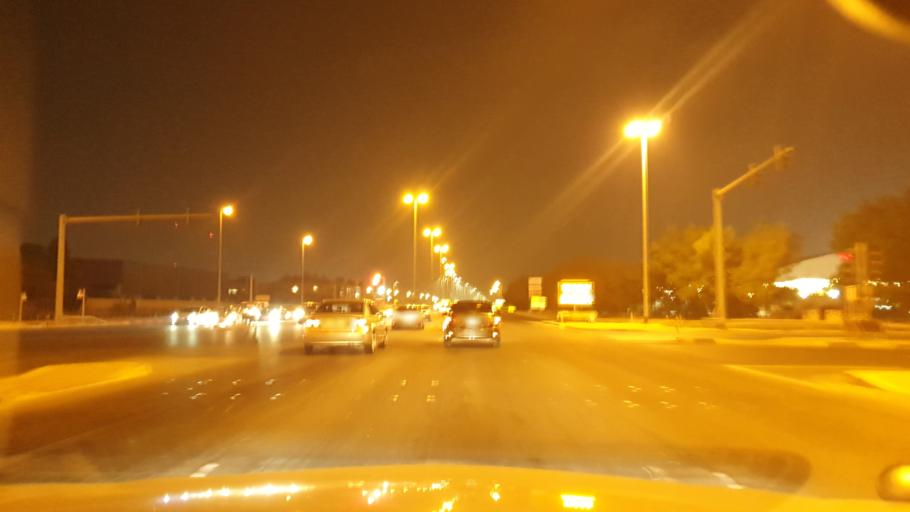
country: BH
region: Northern
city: Madinat `Isa
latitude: 26.1571
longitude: 50.5413
